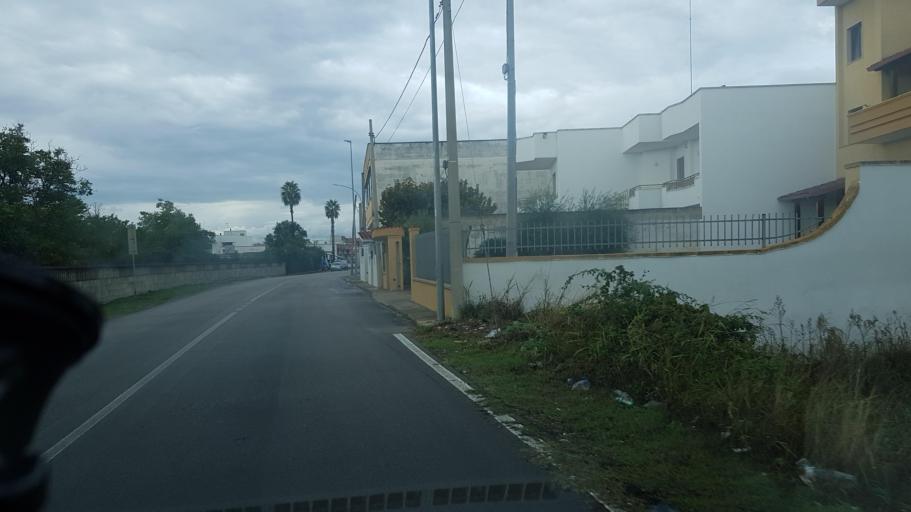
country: IT
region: Apulia
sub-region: Provincia di Lecce
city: Guagnano
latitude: 40.3942
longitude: 17.9558
